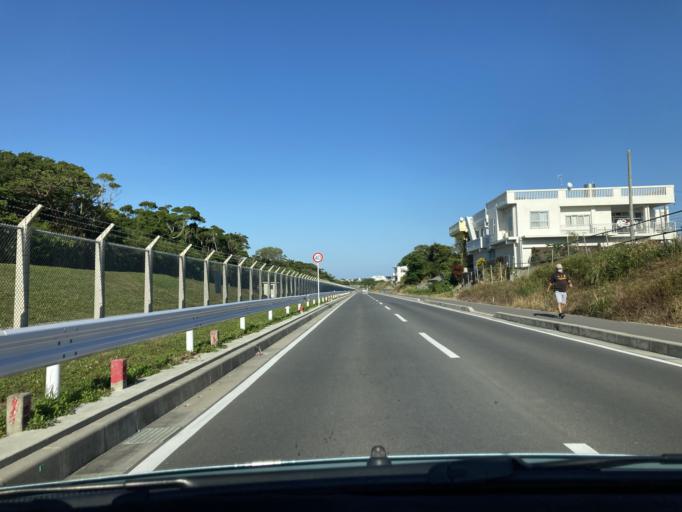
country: JP
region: Okinawa
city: Ginowan
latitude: 26.2716
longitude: 127.7655
